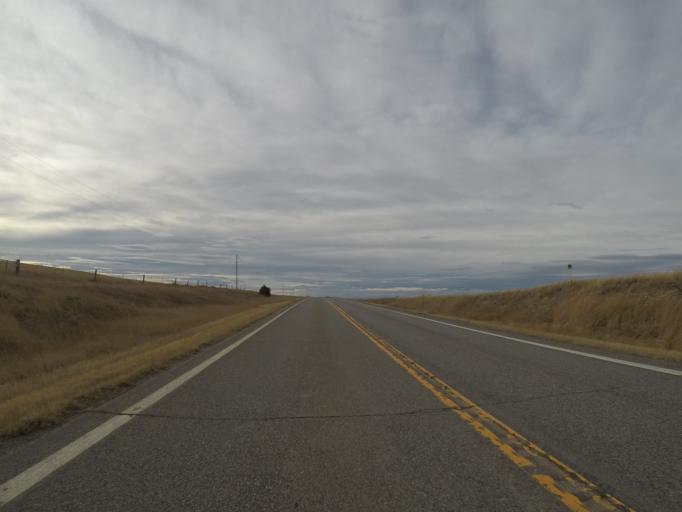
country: US
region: Montana
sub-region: Yellowstone County
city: Laurel
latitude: 45.8565
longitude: -108.7660
